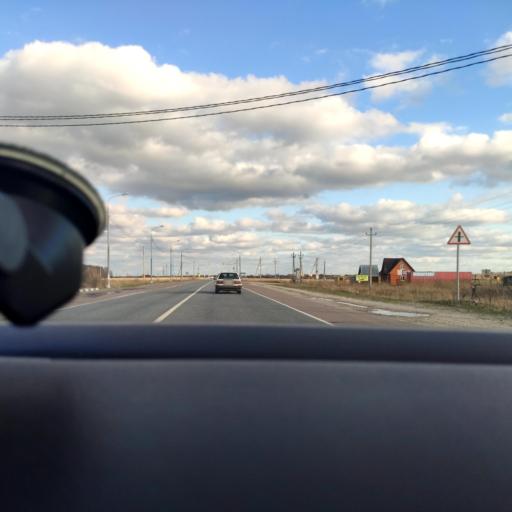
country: RU
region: Moskovskaya
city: Yegor'yevsk
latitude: 55.4047
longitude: 39.0562
